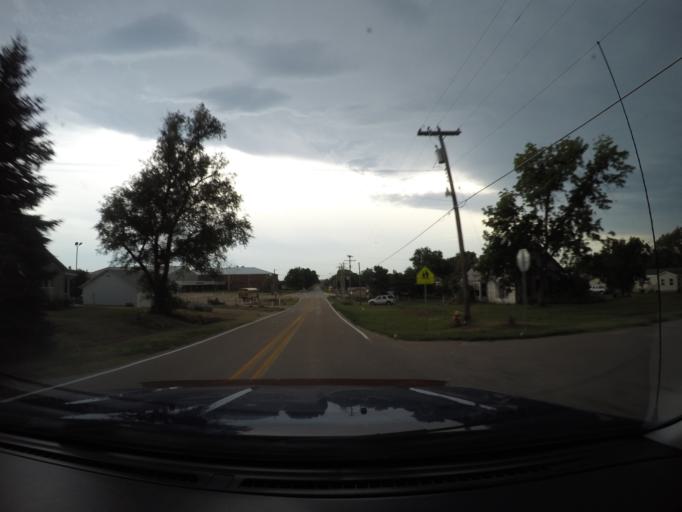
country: US
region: Nebraska
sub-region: Buffalo County
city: Kearney
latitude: 40.8393
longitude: -99.2661
